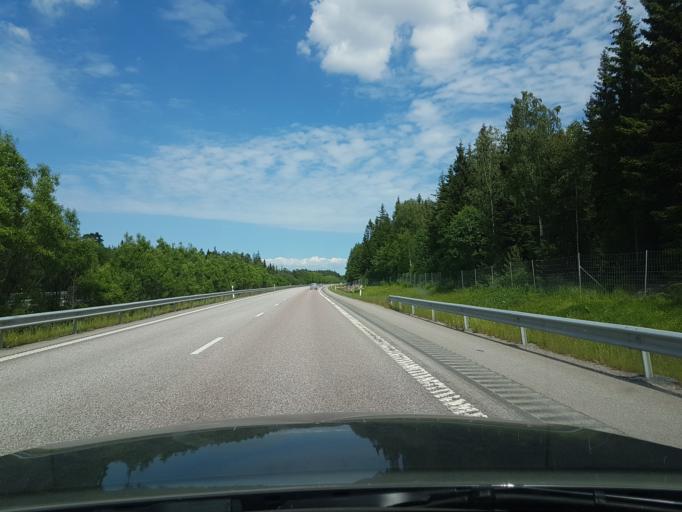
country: SE
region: Stockholm
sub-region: Norrtalje Kommun
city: Rimbo
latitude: 59.6570
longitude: 18.3650
